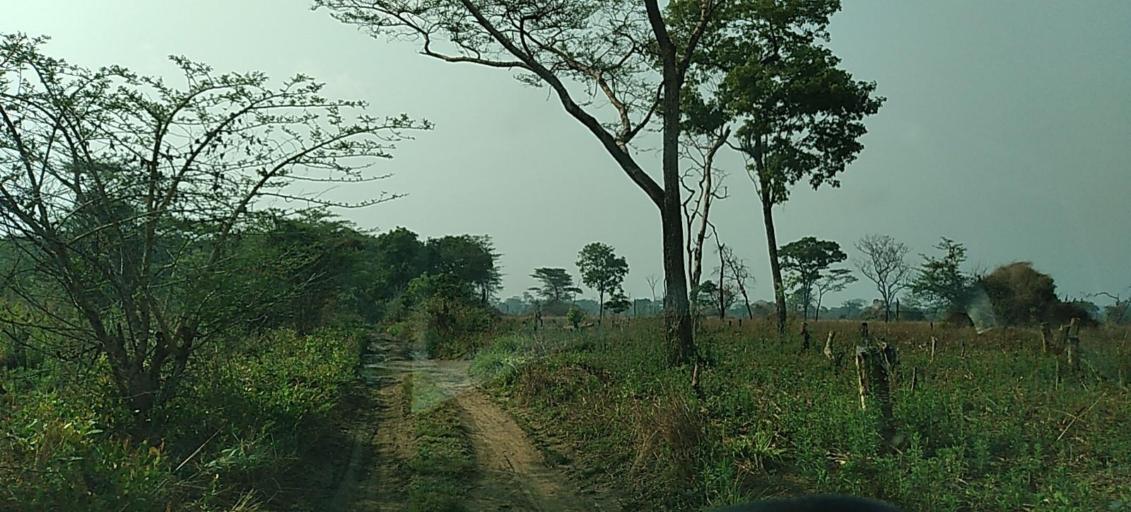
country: ZM
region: North-Western
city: Solwezi
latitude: -12.3739
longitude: 26.5608
